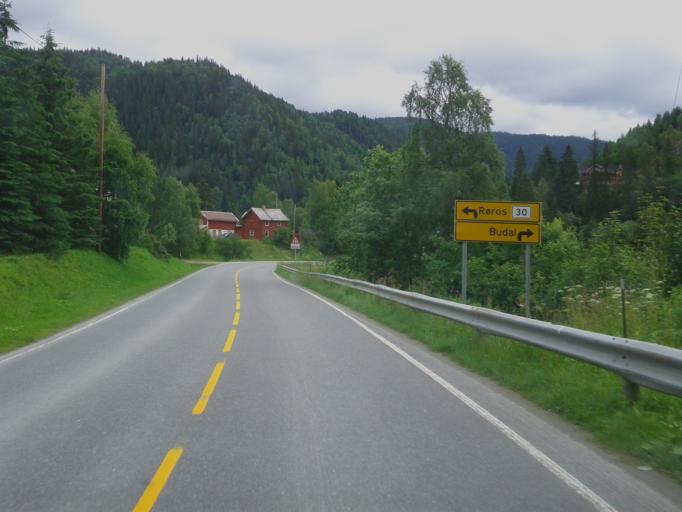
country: NO
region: Sor-Trondelag
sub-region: Midtre Gauldal
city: Storen
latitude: 62.9926
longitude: 10.4937
